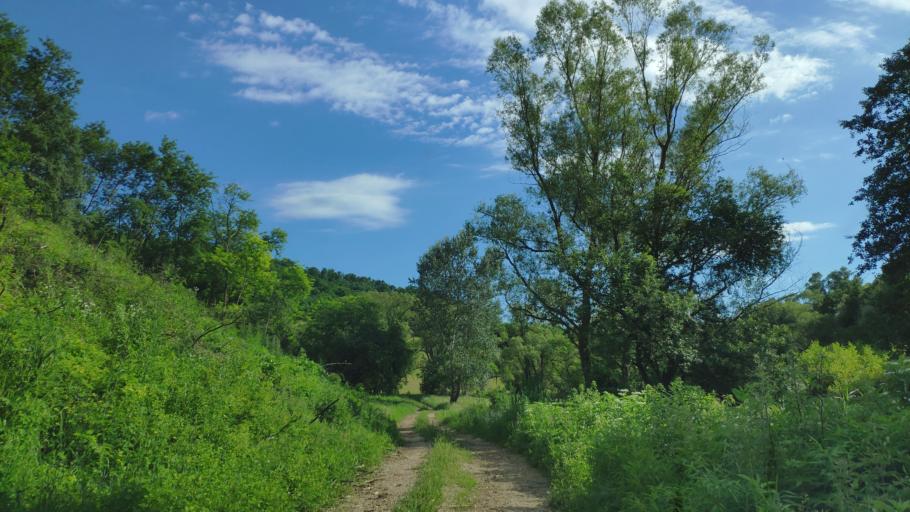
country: SK
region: Banskobystricky
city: Rimavska Sobota
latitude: 48.2542
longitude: 20.1099
